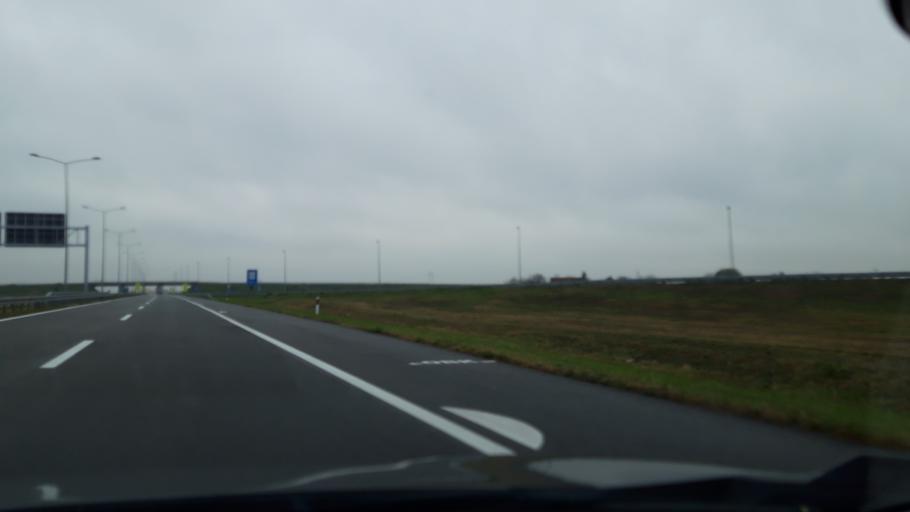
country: RS
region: Autonomna Pokrajina Vojvodina
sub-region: Severnobacki Okrug
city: Subotica
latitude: 46.0296
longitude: 19.7373
